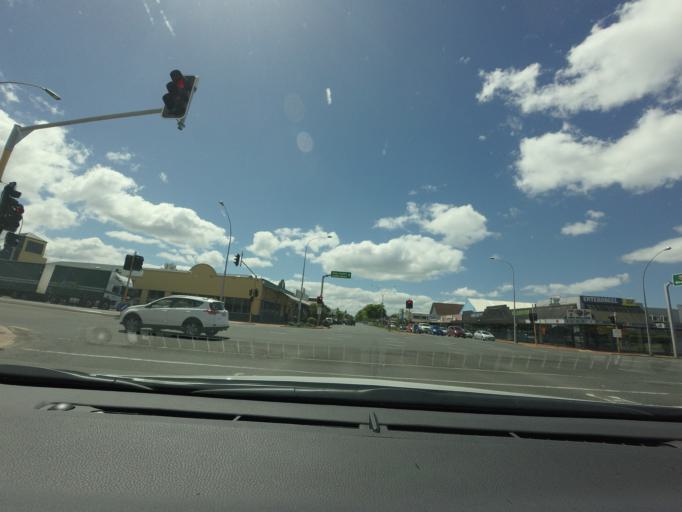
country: NZ
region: Bay of Plenty
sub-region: Rotorua District
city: Rotorua
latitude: -38.1401
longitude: 176.2537
